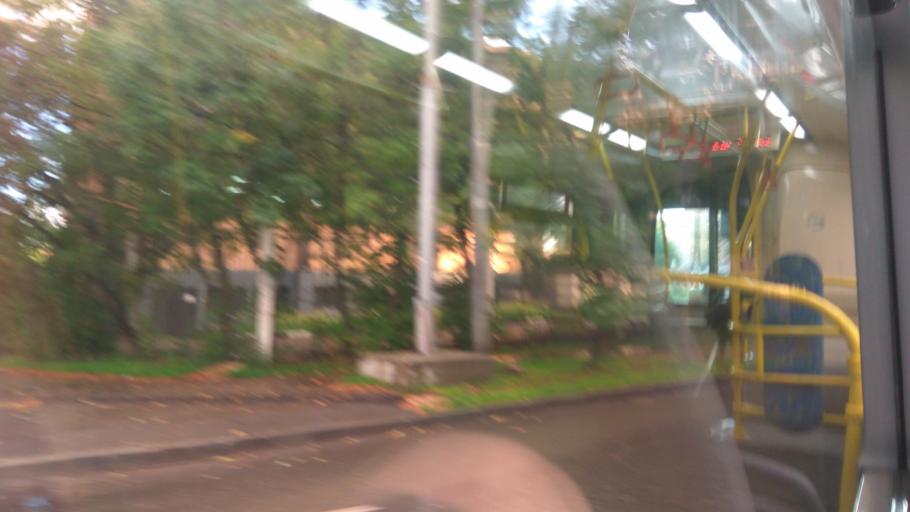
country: RU
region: Moskovskaya
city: Bol'shaya Setun'
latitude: 55.7232
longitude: 37.4062
